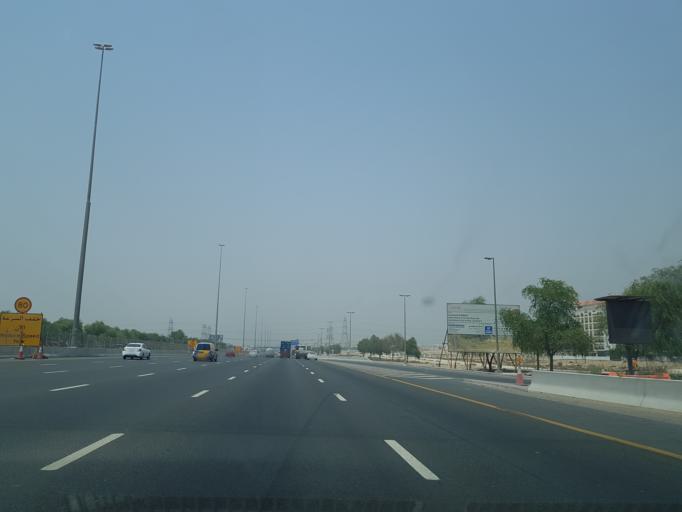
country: AE
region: Ash Shariqah
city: Sharjah
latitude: 25.1498
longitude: 55.3875
